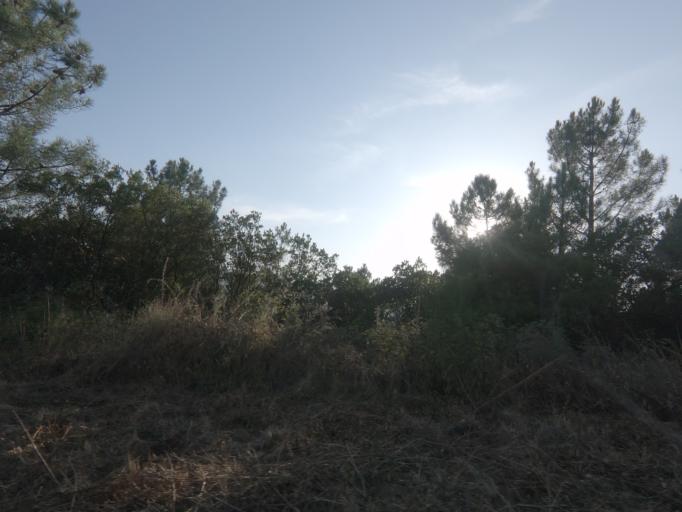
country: PT
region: Vila Real
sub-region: Sabrosa
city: Sabrosa
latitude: 41.2669
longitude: -7.5328
